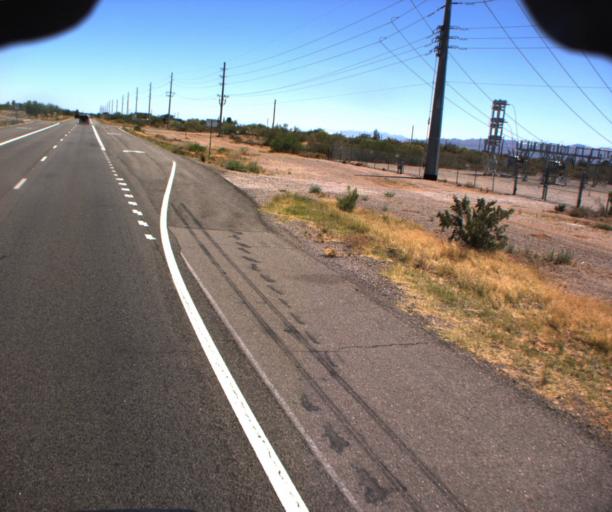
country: US
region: Arizona
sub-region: Maricopa County
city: Wickenburg
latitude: 33.8352
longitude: -112.6043
